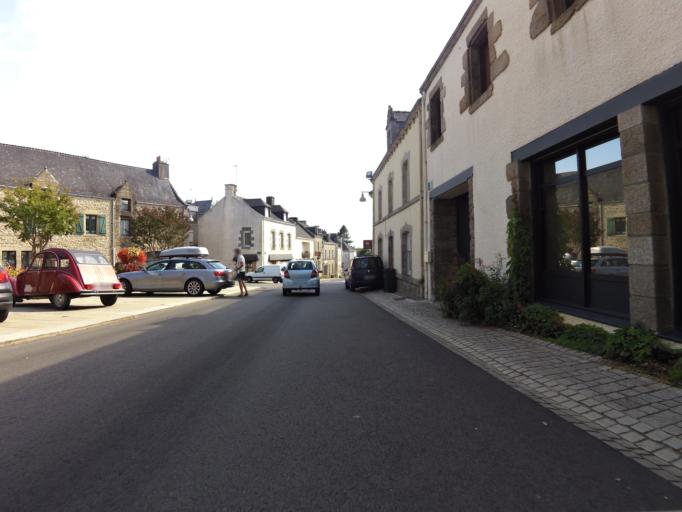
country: FR
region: Brittany
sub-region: Departement du Morbihan
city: Limerzel
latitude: 47.6361
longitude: -2.3541
